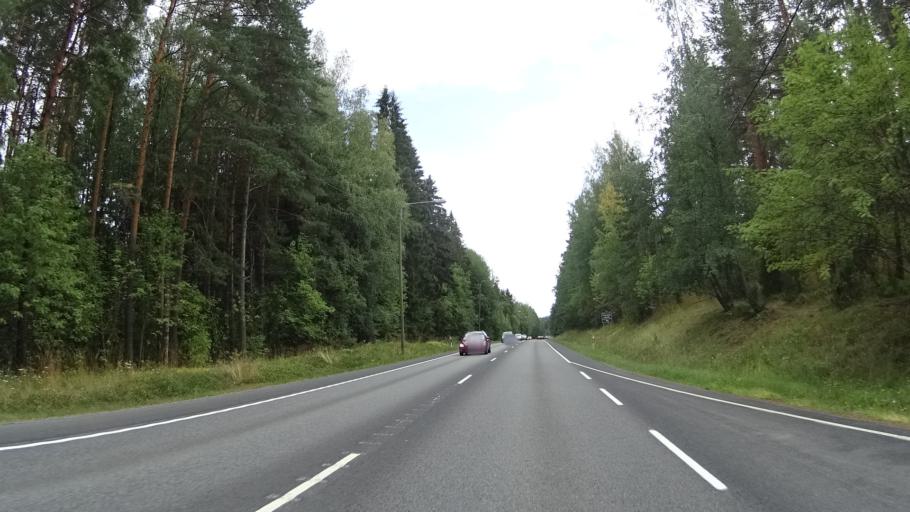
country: FI
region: Pirkanmaa
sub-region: Tampere
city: Kangasala
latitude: 61.4284
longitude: 24.1320
